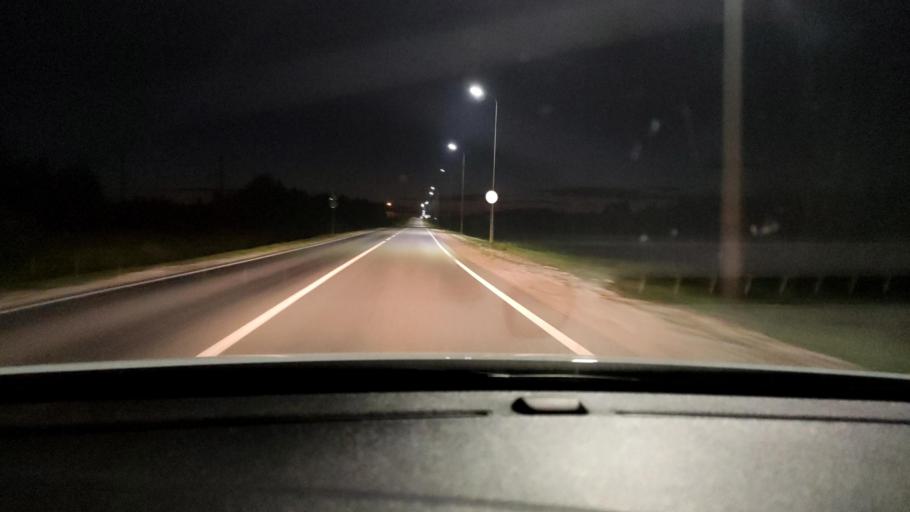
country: RU
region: Tatarstan
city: Sviyazhsk
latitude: 55.7252
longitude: 48.7488
